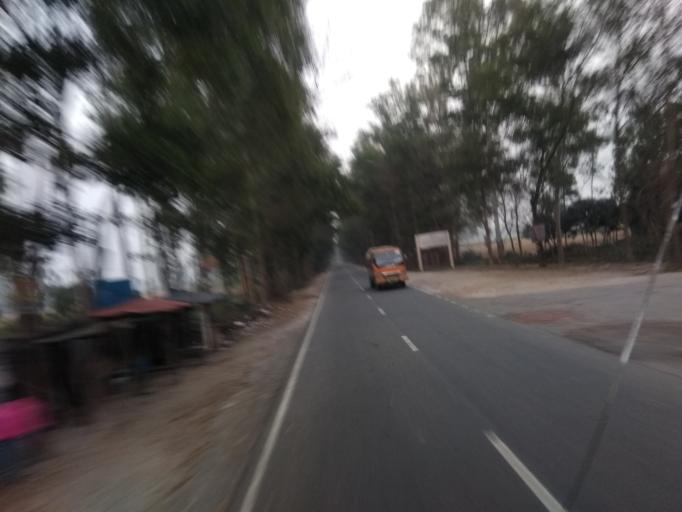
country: BD
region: Rajshahi
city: Bogra
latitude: 24.6658
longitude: 89.2727
